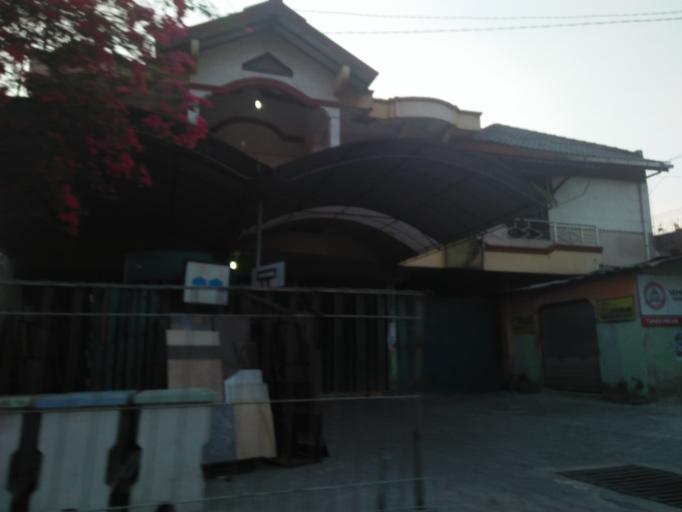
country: ID
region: Daerah Istimewa Yogyakarta
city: Sewon
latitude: -7.8558
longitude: 110.4095
